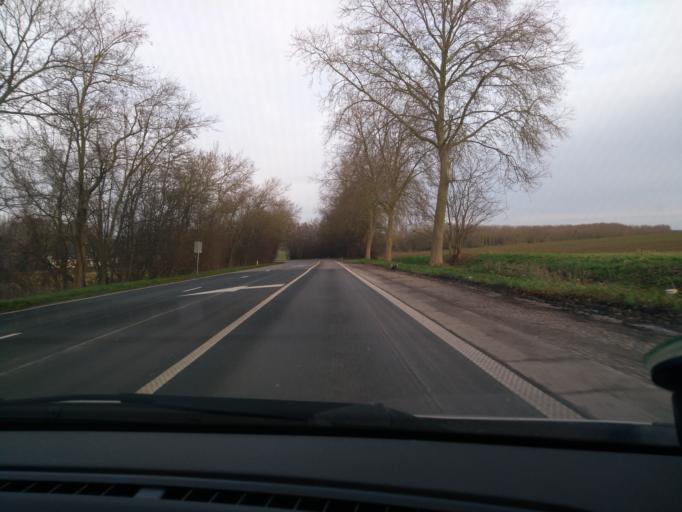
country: BE
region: Wallonia
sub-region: Province du Hainaut
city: Quevy-le-Petit
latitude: 50.3736
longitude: 3.9680
